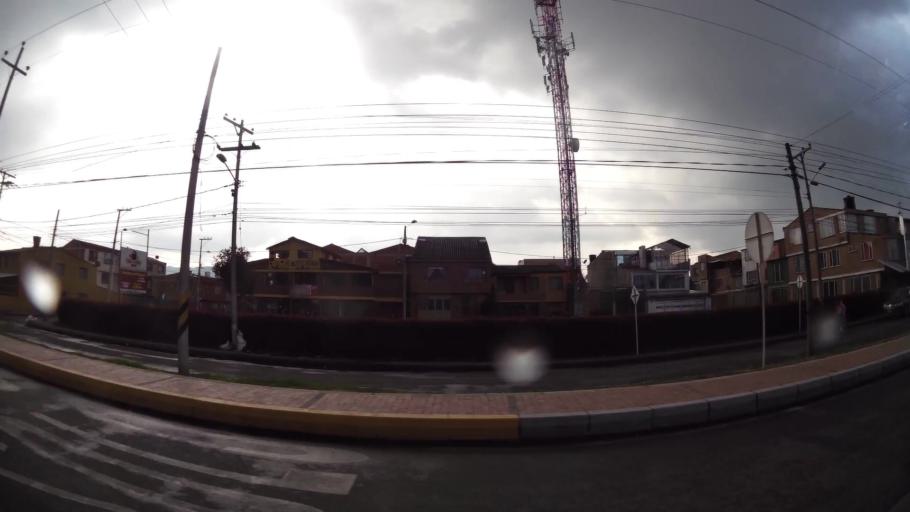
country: CO
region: Cundinamarca
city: Chia
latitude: 4.8526
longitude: -74.0497
